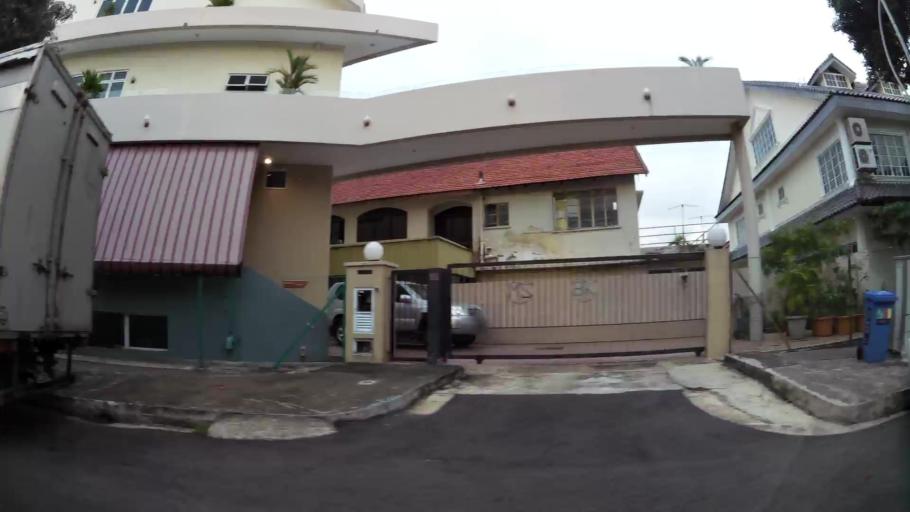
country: SG
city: Singapore
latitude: 1.3312
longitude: 103.8747
